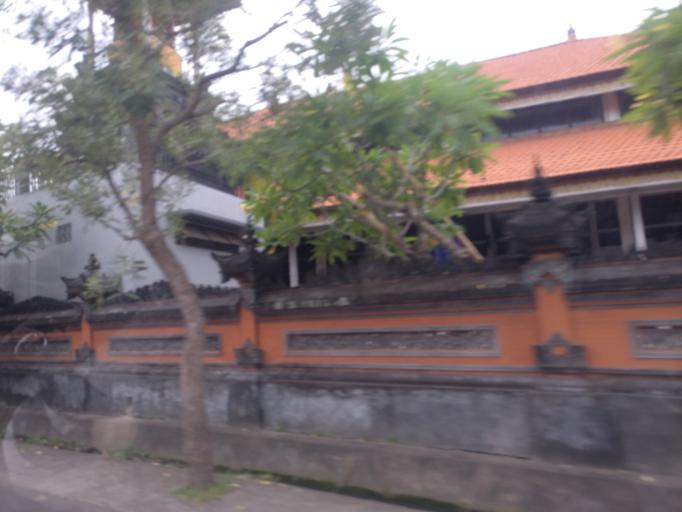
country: ID
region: Bali
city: Banjar Desa
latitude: -8.5734
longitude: 115.2967
